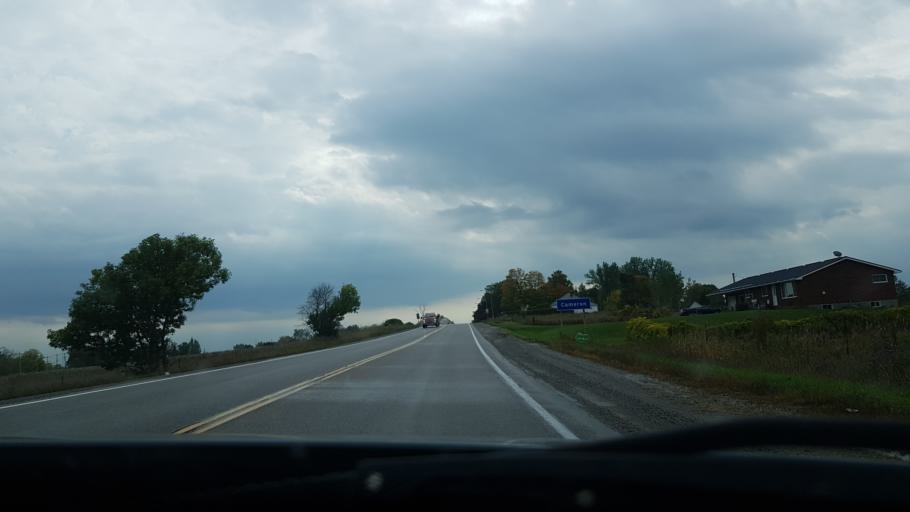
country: CA
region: Ontario
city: Omemee
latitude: 44.4449
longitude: -78.7703
